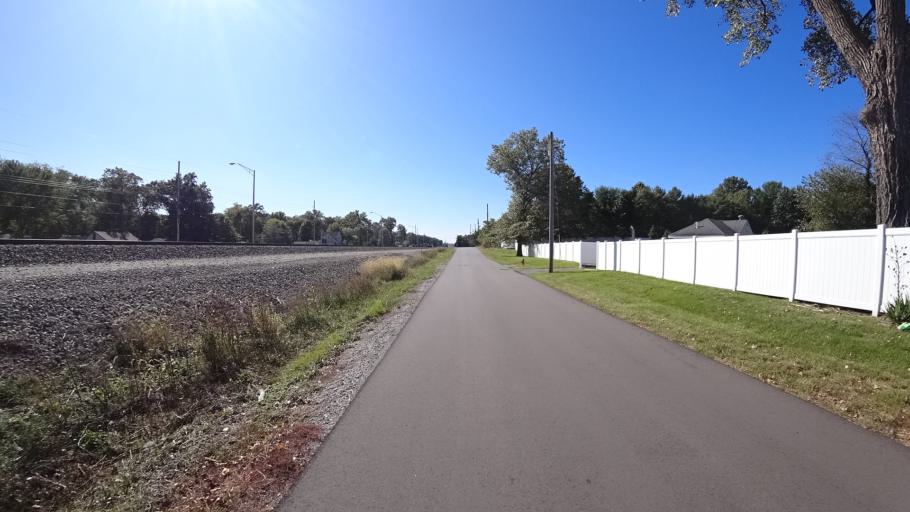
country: US
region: Indiana
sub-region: LaPorte County
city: Long Beach
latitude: 41.7453
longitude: -86.8286
